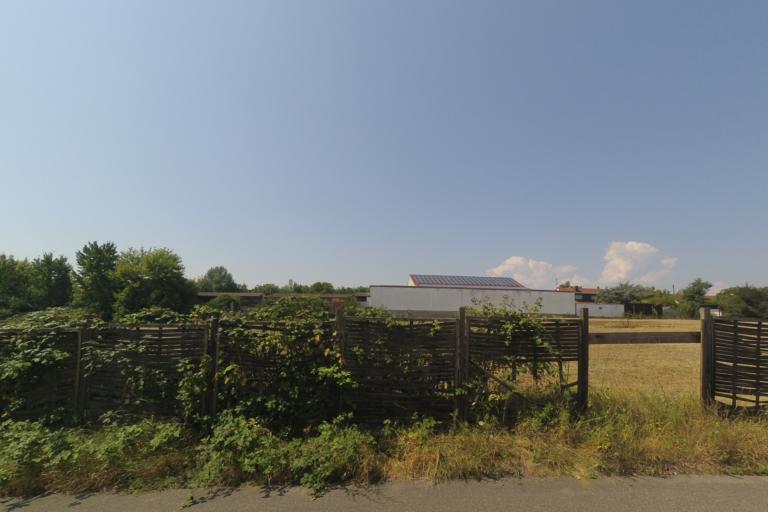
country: DE
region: Rheinland-Pfalz
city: Gartenstadt
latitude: 49.4811
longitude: 8.3688
